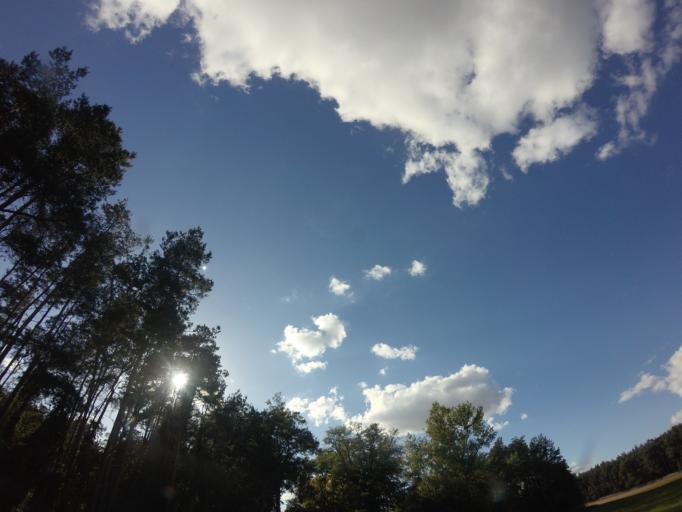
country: PL
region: Greater Poland Voivodeship
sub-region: Powiat koscianski
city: Smigiel
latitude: 52.0607
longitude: 16.4642
